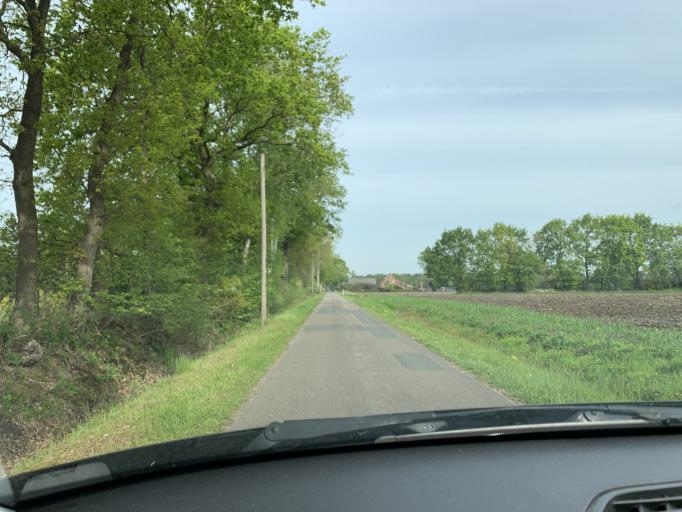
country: DE
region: Lower Saxony
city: Apen
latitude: 53.2318
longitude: 7.8404
